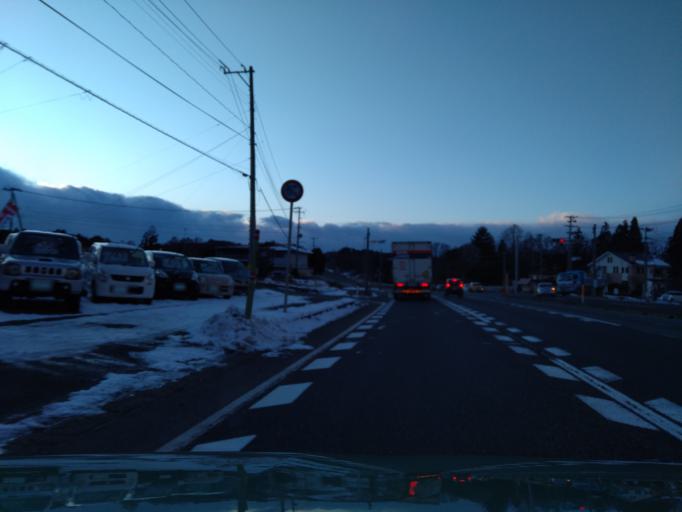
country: JP
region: Iwate
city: Shizukuishi
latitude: 39.7016
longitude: 141.0481
